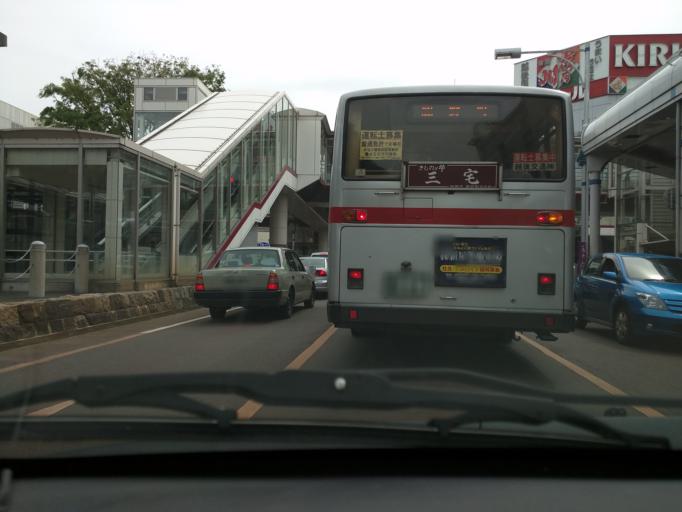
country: JP
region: Niigata
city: Nagaoka
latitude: 37.4475
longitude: 138.8527
